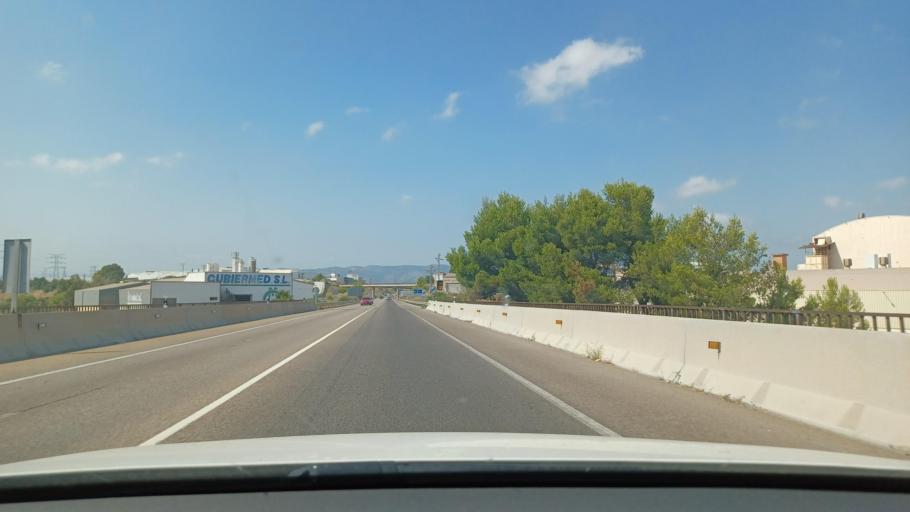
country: ES
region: Valencia
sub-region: Provincia de Castello
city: Vila-real
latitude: 39.9545
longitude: -0.0854
